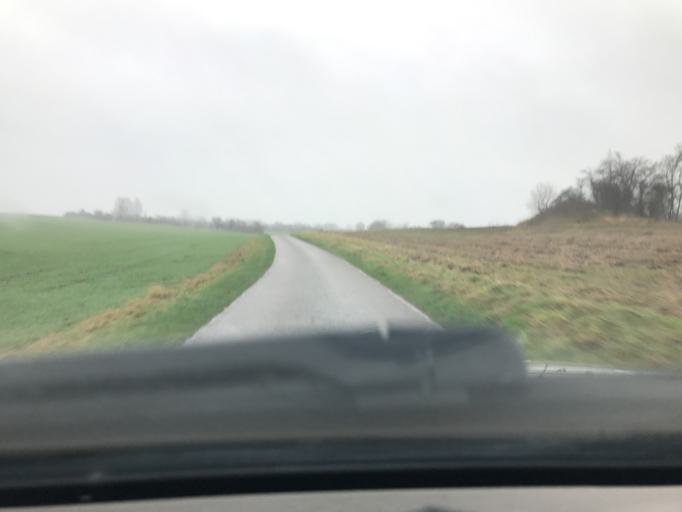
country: DE
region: Schleswig-Holstein
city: Pommerby
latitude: 54.8853
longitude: 10.0596
